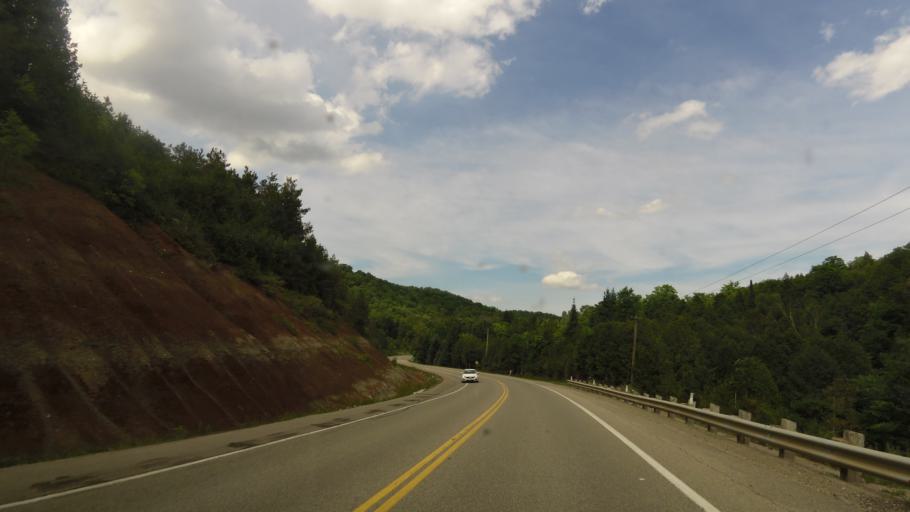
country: CA
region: Ontario
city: Orangeville
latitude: 43.9613
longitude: -80.0750
